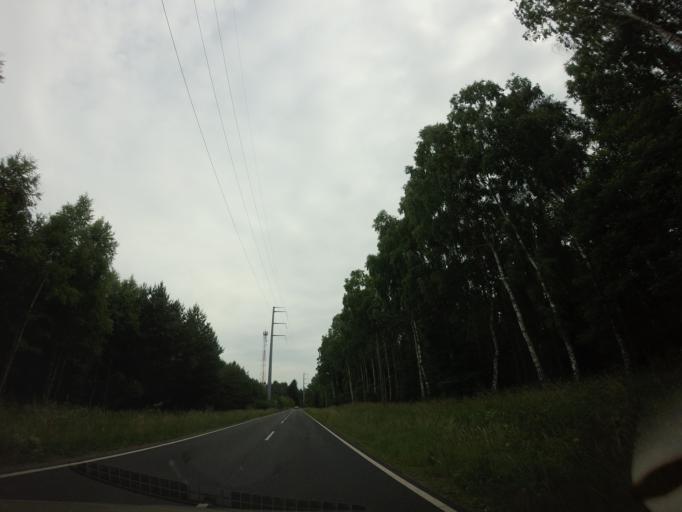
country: PL
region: West Pomeranian Voivodeship
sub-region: Powiat drawski
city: Wierzchowo
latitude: 53.4393
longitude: 16.2072
